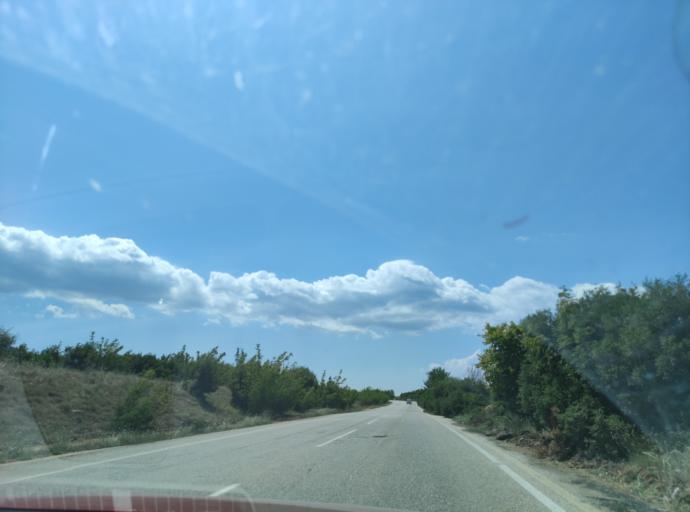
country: GR
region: East Macedonia and Thrace
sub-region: Nomos Kavalas
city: Nikisiani
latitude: 40.9911
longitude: 24.0804
